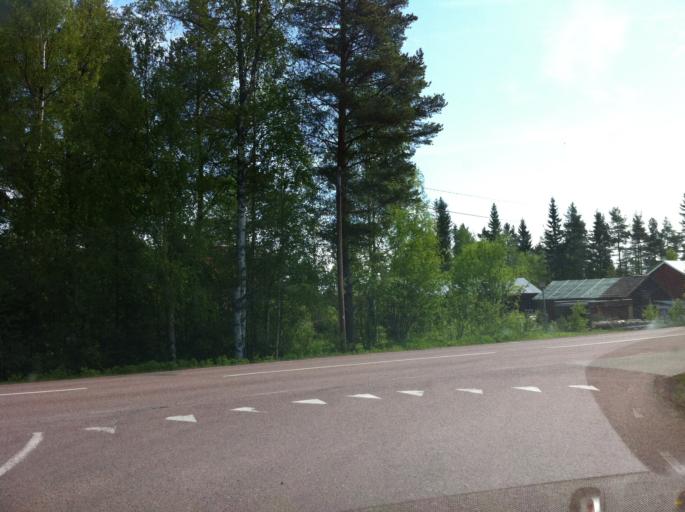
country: SE
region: Dalarna
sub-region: Mora Kommun
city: Mora
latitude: 60.8873
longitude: 14.5264
